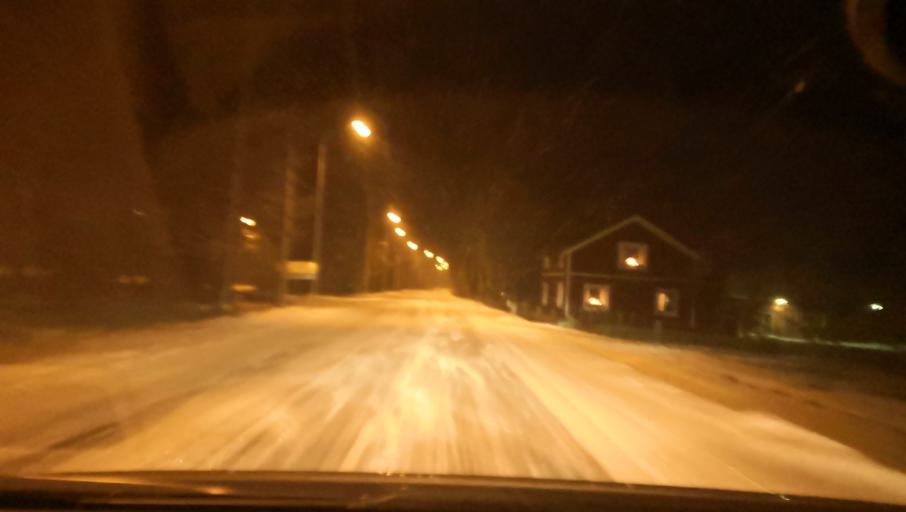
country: SE
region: Uppsala
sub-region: Heby Kommun
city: Tarnsjo
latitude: 60.1484
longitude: 16.9186
